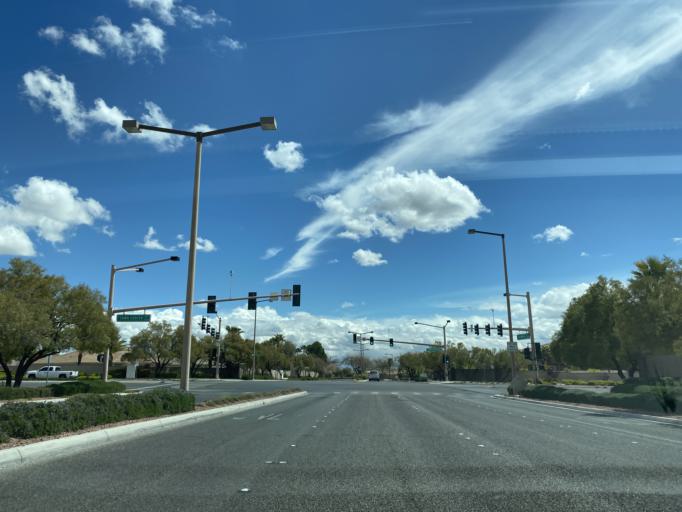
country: US
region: Nevada
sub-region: Clark County
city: Summerlin South
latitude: 36.1331
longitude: -115.3256
